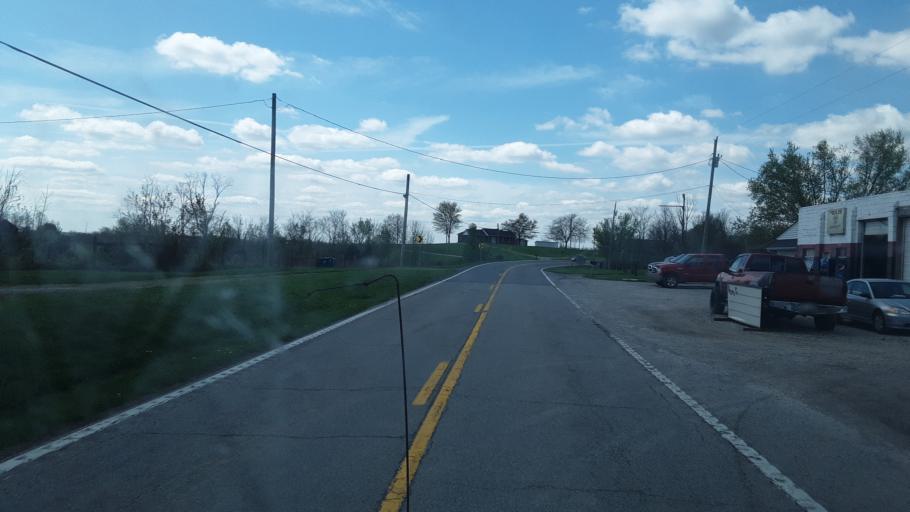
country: US
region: Kentucky
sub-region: Grant County
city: Dry Ridge
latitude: 38.6660
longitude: -84.6409
